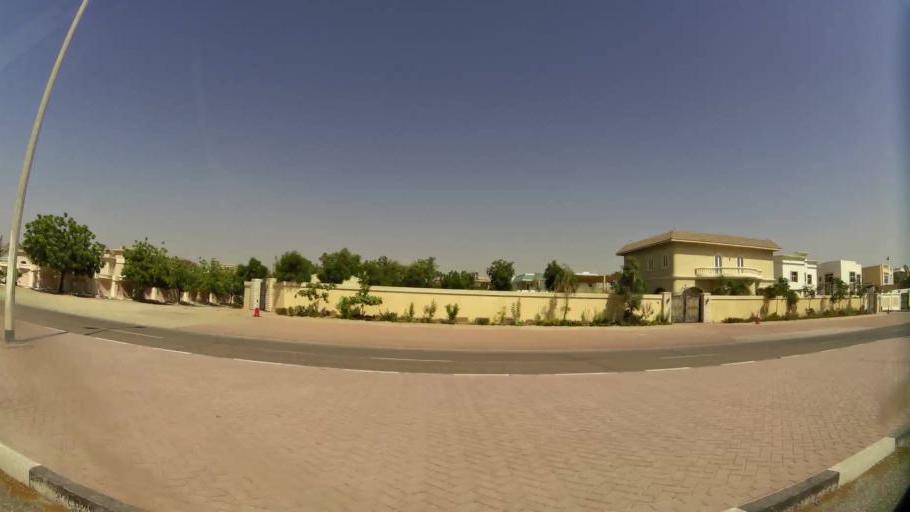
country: AE
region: Ajman
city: Ajman
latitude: 25.4083
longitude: 55.4783
